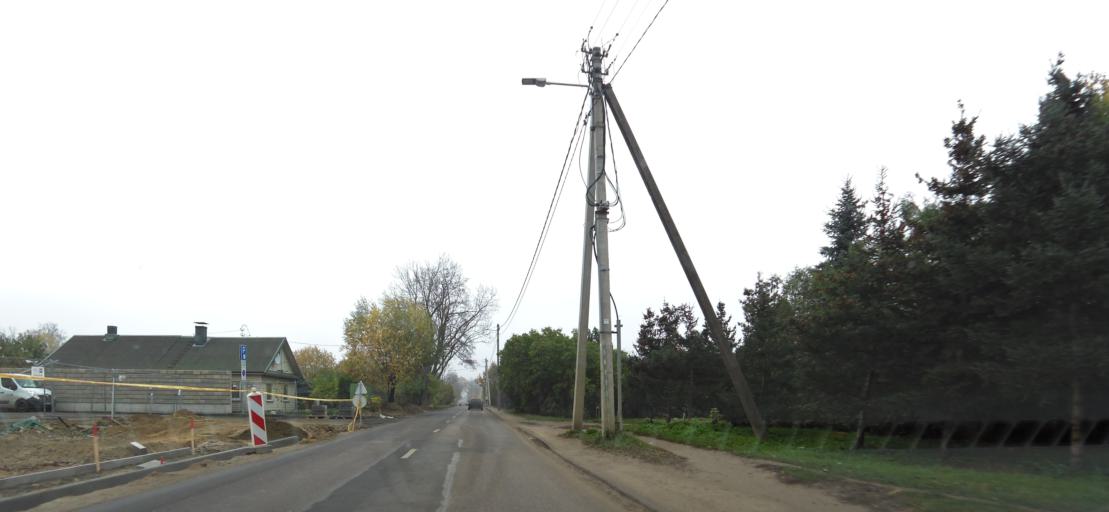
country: LT
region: Vilnius County
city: Rasos
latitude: 54.6623
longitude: 25.3436
